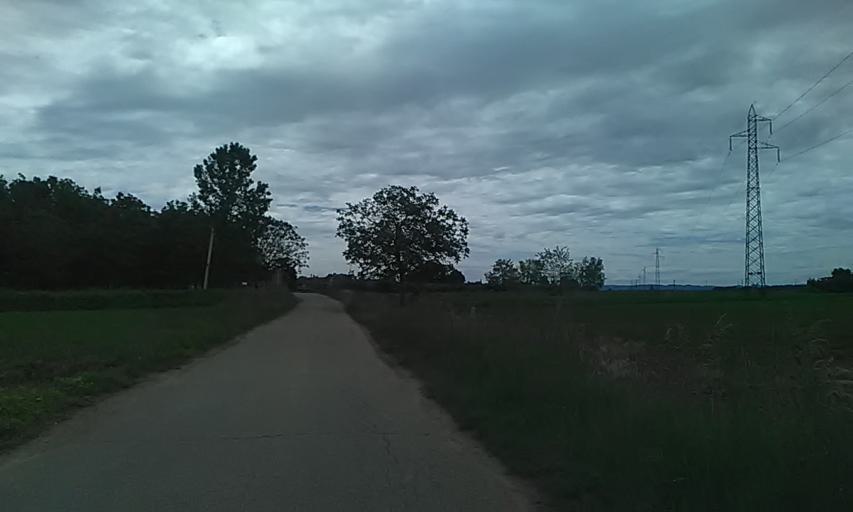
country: IT
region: Piedmont
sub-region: Provincia di Vercelli
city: Borgo d'Ale
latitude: 45.3225
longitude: 8.0492
